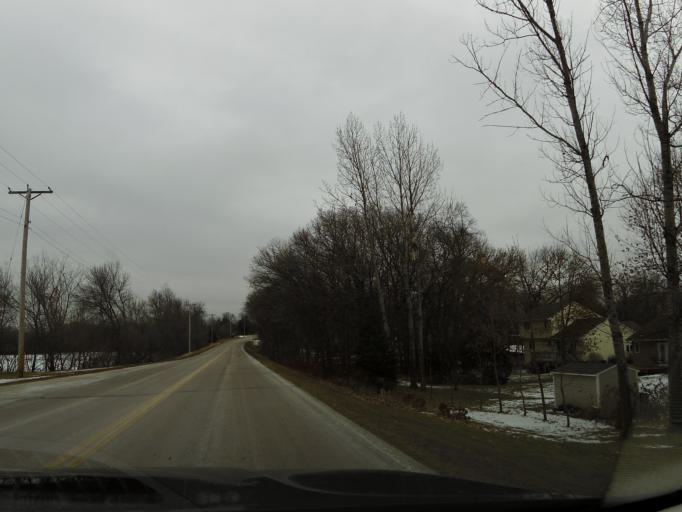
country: US
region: Minnesota
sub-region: Carver County
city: Watertown
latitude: 44.9588
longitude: -93.8362
